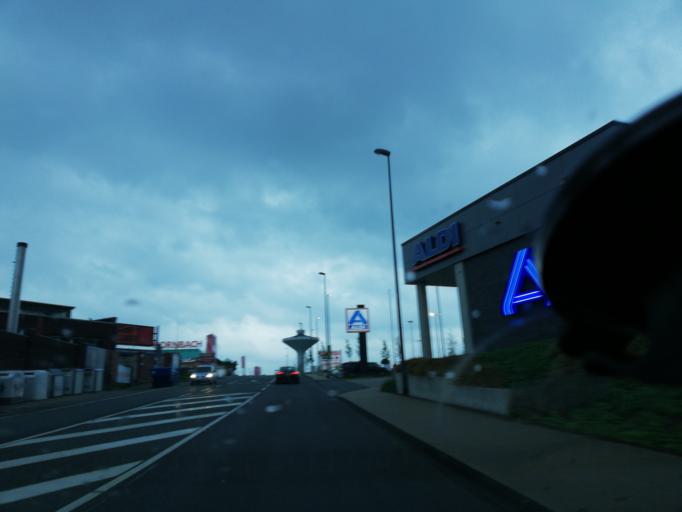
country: DE
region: North Rhine-Westphalia
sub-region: Regierungsbezirk Dusseldorf
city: Wuppertal
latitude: 51.2467
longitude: 7.1878
